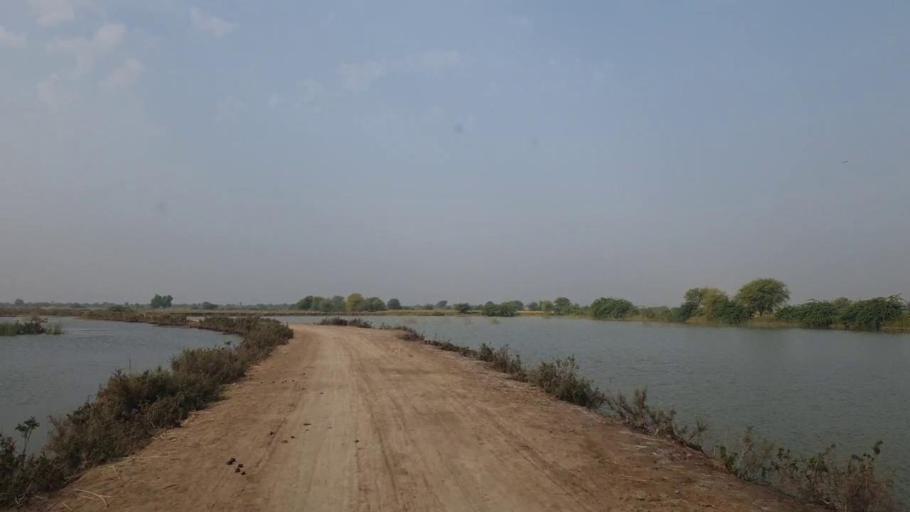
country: PK
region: Sindh
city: Talhar
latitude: 24.8438
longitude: 68.8094
